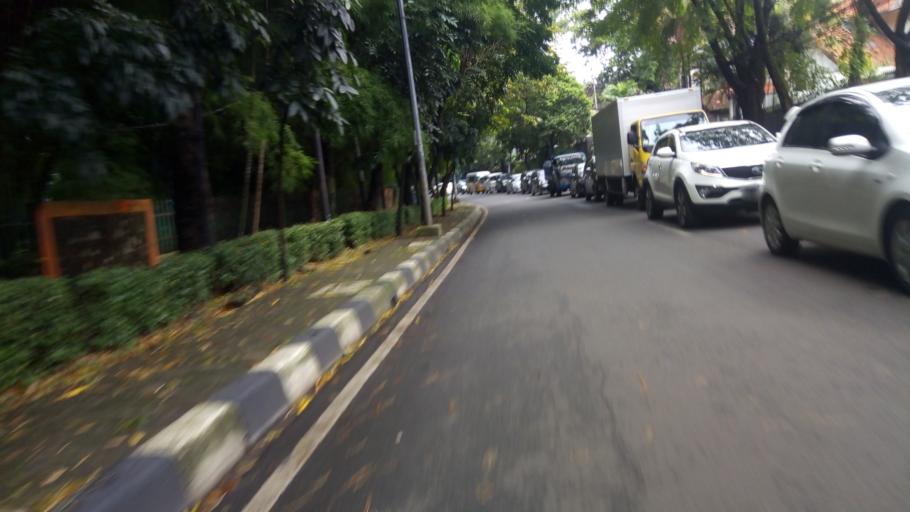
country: ID
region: Jakarta Raya
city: Jakarta
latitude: -6.2483
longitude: 106.8051
